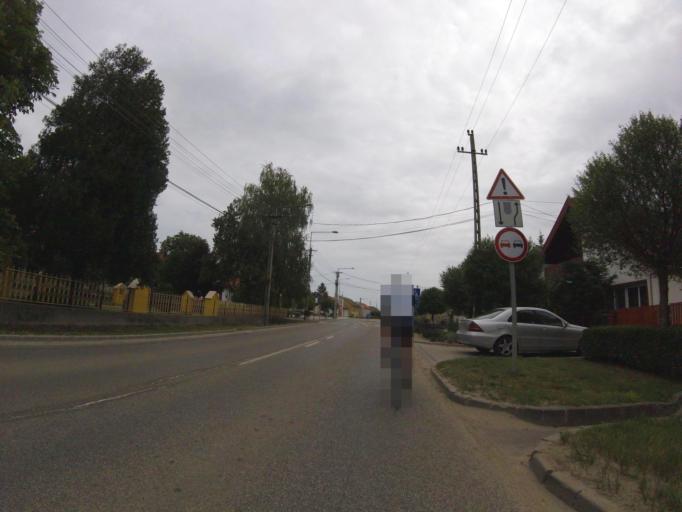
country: HU
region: Pest
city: Ocsa
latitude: 47.2931
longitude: 19.2263
